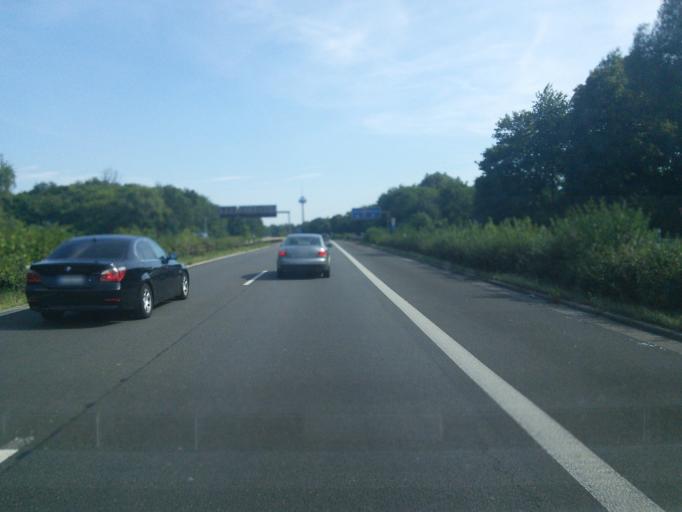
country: DE
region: North Rhine-Westphalia
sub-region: Regierungsbezirk Koln
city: Bilderstoeckchen
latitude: 50.9714
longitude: 6.9184
